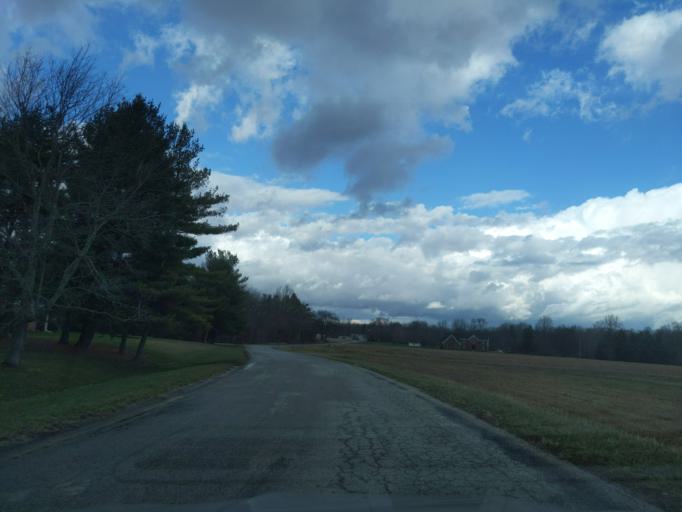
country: US
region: Indiana
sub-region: Decatur County
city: Saint Paul
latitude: 39.4070
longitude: -85.5587
